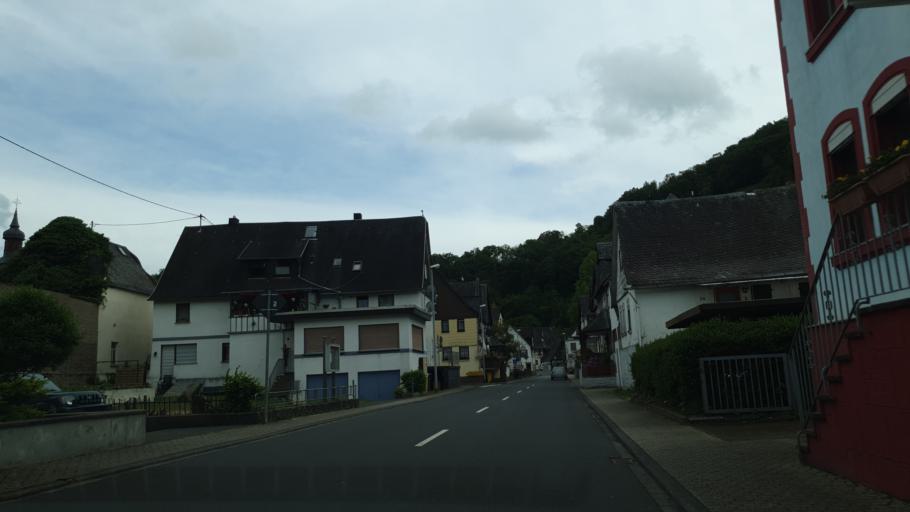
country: DE
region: Rheinland-Pfalz
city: Obernhof
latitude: 50.3200
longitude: 7.8434
